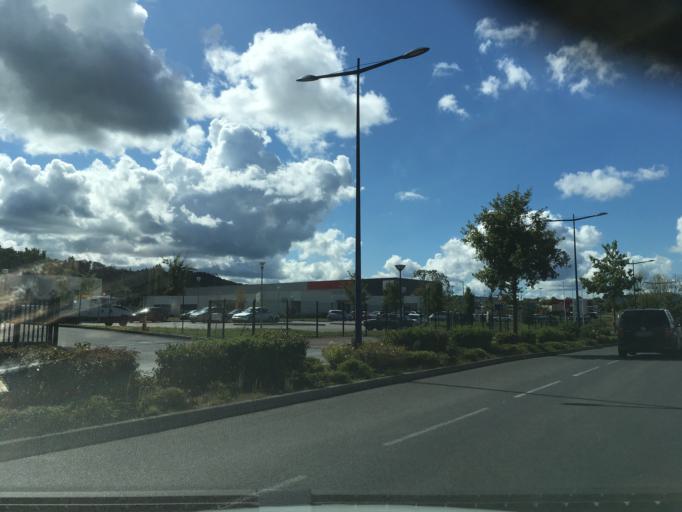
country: FR
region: Limousin
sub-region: Departement de la Correze
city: Saint-Pantaleon-de-Larche
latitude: 45.1396
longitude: 1.4746
